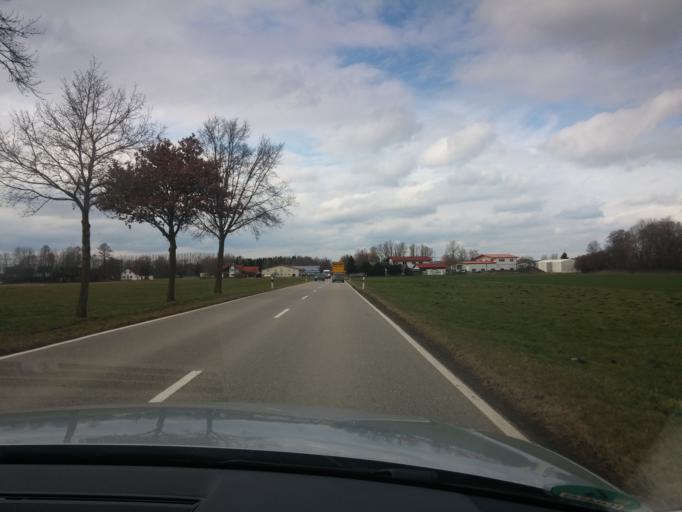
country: DE
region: Bavaria
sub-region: Swabia
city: Benningen
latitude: 47.9602
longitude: 10.2050
